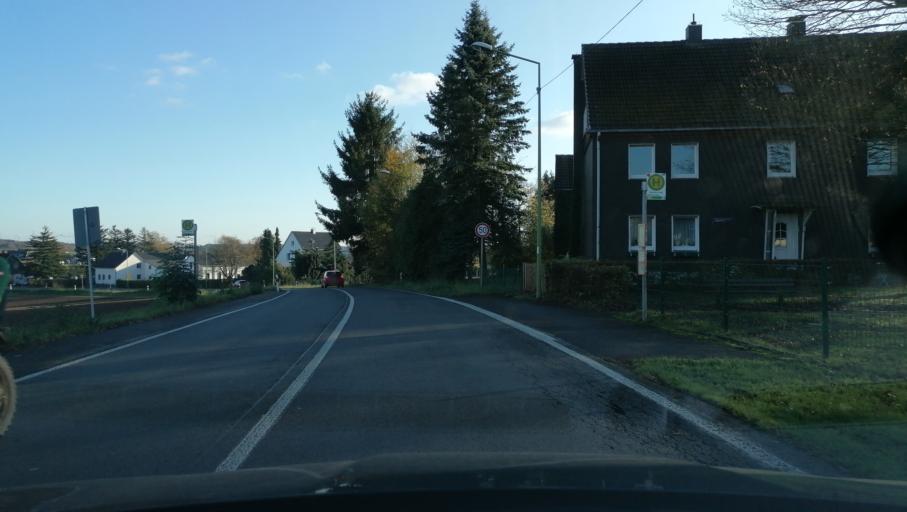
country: DE
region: North Rhine-Westphalia
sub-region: Regierungsbezirk Arnsberg
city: Schwelm
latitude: 51.2649
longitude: 7.3248
